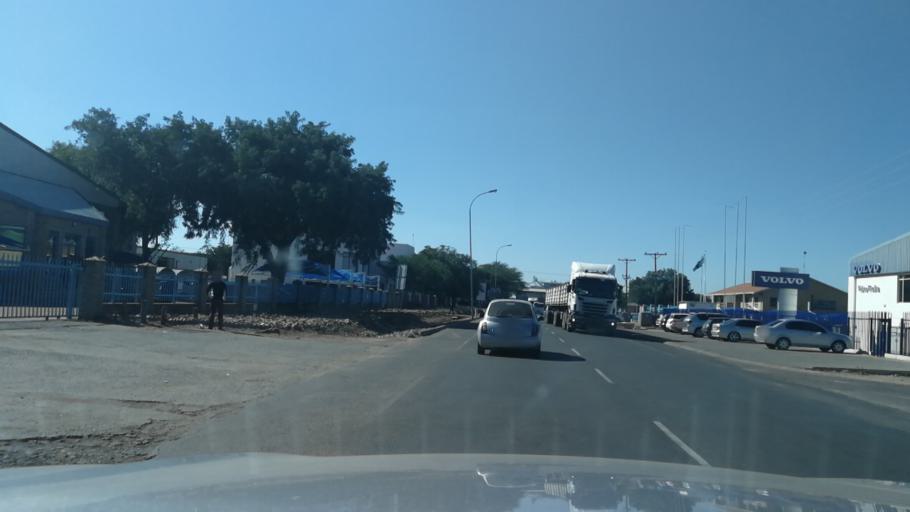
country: BW
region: South East
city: Gaborone
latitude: -24.6926
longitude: 25.8853
